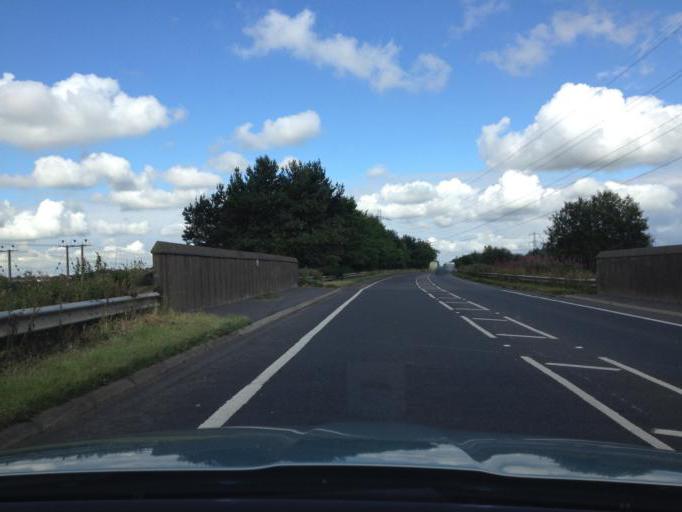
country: GB
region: Scotland
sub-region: West Lothian
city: Whitburn
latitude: 55.8880
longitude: -3.6738
